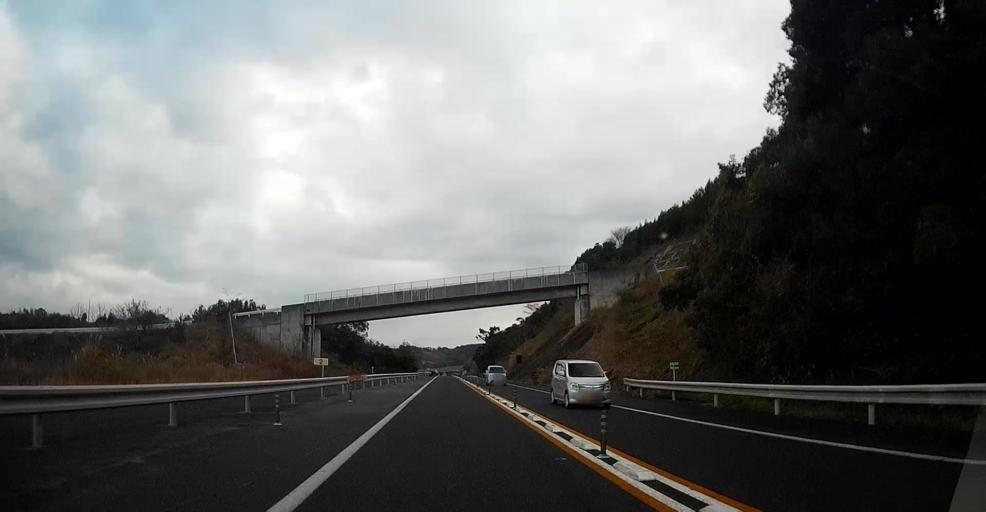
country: JP
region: Kumamoto
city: Hondo
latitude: 32.5094
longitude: 130.3256
